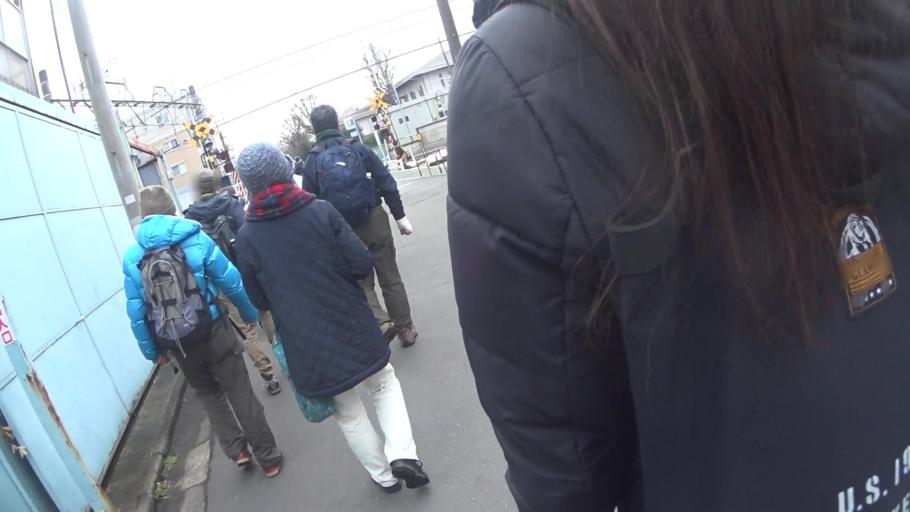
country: JP
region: Tokyo
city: Musashino
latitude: 35.7254
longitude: 139.6019
